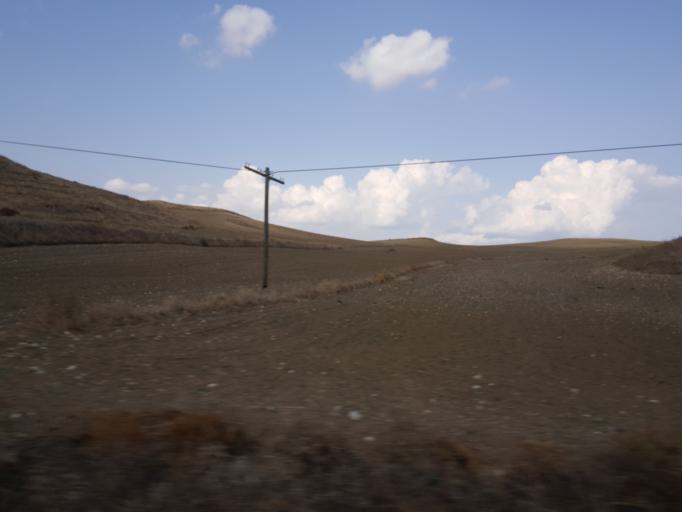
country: TR
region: Corum
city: Bogazkale
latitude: 40.1393
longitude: 34.5661
